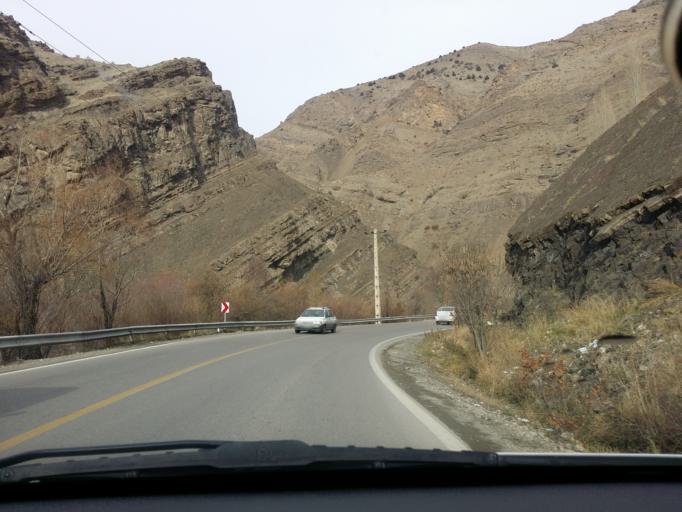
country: IR
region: Tehran
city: Tajrish
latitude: 36.0166
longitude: 51.2794
